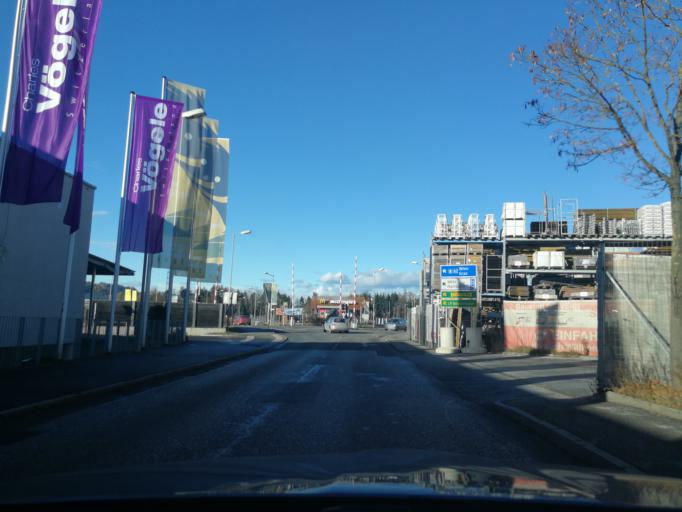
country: AT
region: Styria
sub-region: Politischer Bezirk Weiz
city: Gleisdorf
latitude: 47.1074
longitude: 15.7044
